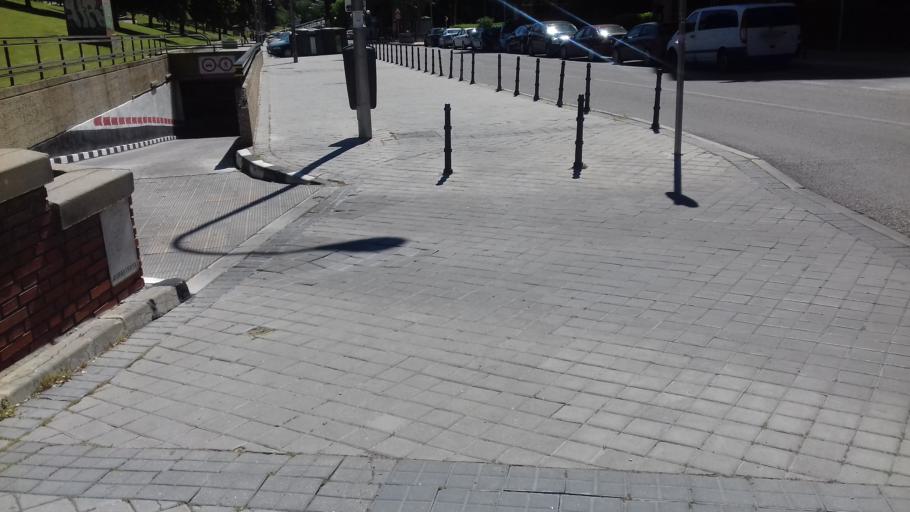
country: ES
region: Madrid
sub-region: Provincia de Madrid
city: Moratalaz
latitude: 40.4142
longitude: -3.6656
